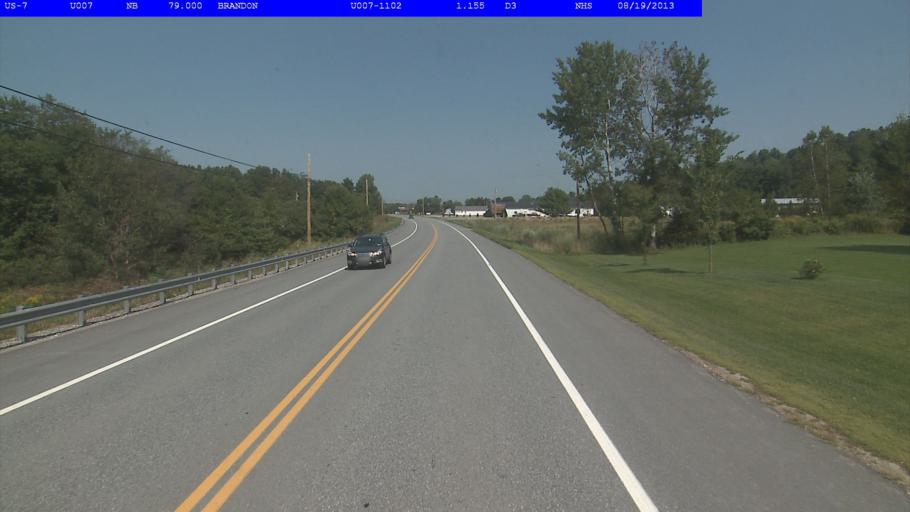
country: US
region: Vermont
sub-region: Rutland County
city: Brandon
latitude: 43.7709
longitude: -73.0515
